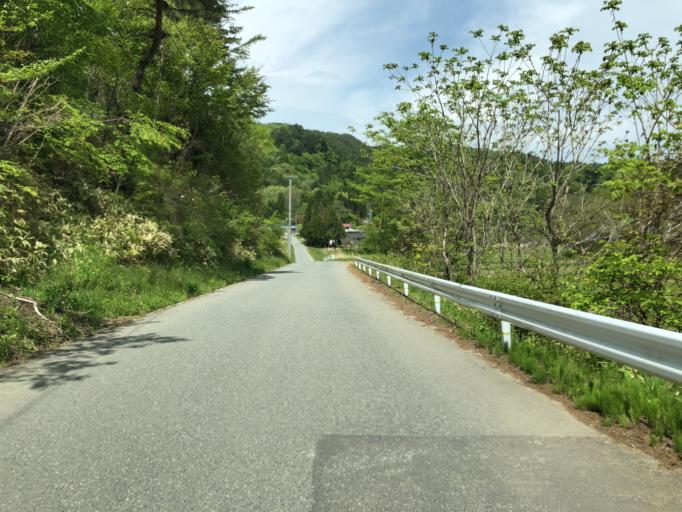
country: JP
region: Fukushima
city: Yanagawamachi-saiwaicho
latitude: 37.7446
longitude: 140.7106
